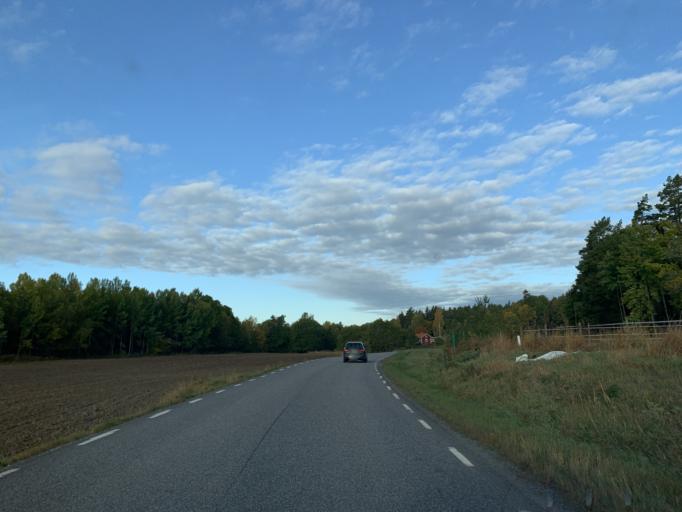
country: SE
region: Stockholm
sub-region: Upplands-Bro Kommun
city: Bro
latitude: 59.5080
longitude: 17.5984
